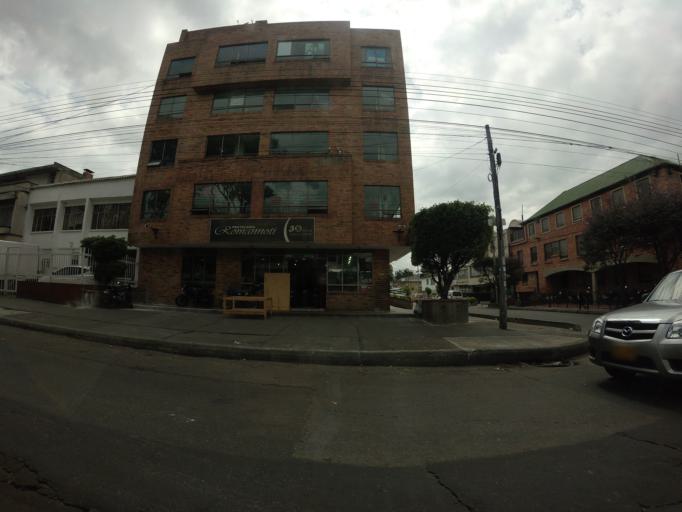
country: CO
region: Bogota D.C.
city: Bogota
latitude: 4.6276
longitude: -74.0775
